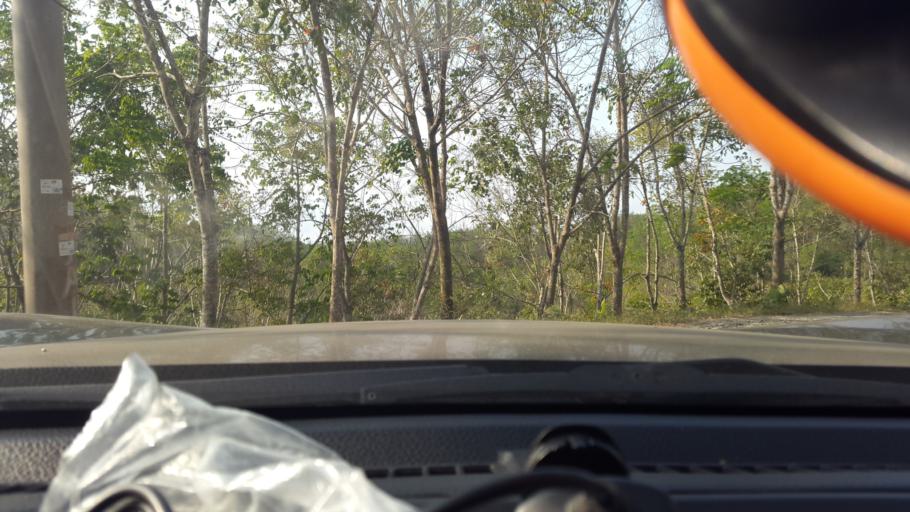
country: ID
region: West Java
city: Cikupa
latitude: -7.3588
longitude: 106.6975
